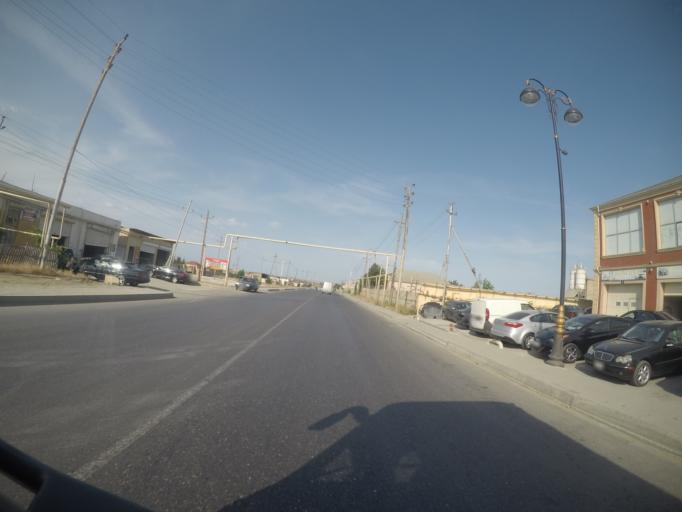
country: AZ
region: Baki
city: Bilajari
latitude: 40.4440
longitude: 49.7904
